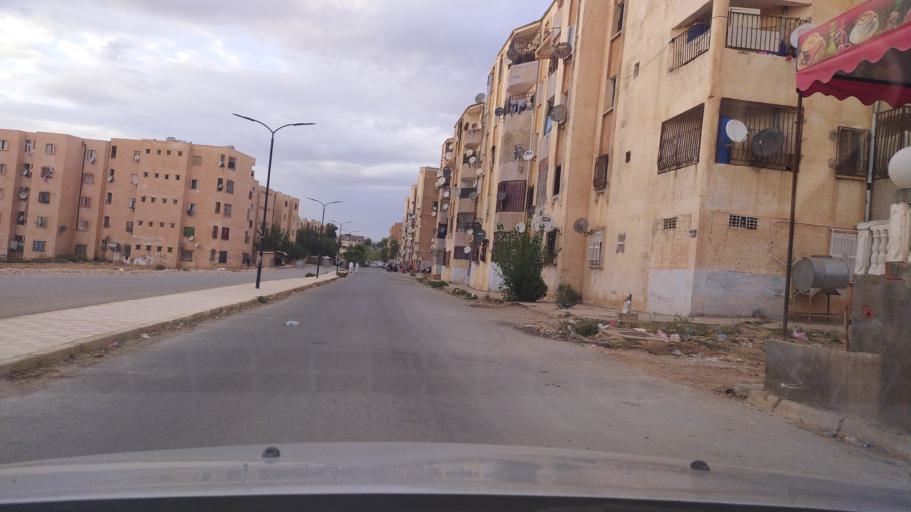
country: DZ
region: Tiaret
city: Frenda
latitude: 35.0551
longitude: 1.0623
